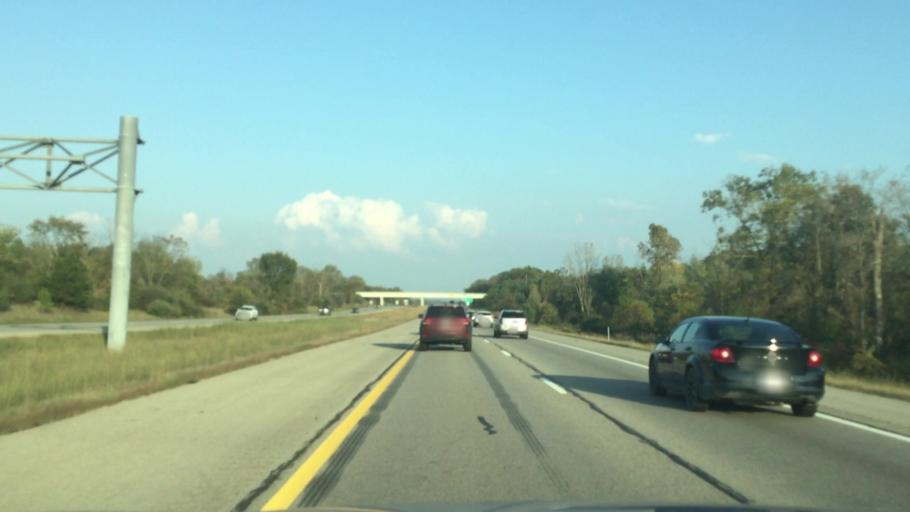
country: US
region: Michigan
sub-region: Washtenaw County
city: Ann Arbor
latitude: 42.3253
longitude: -83.6679
